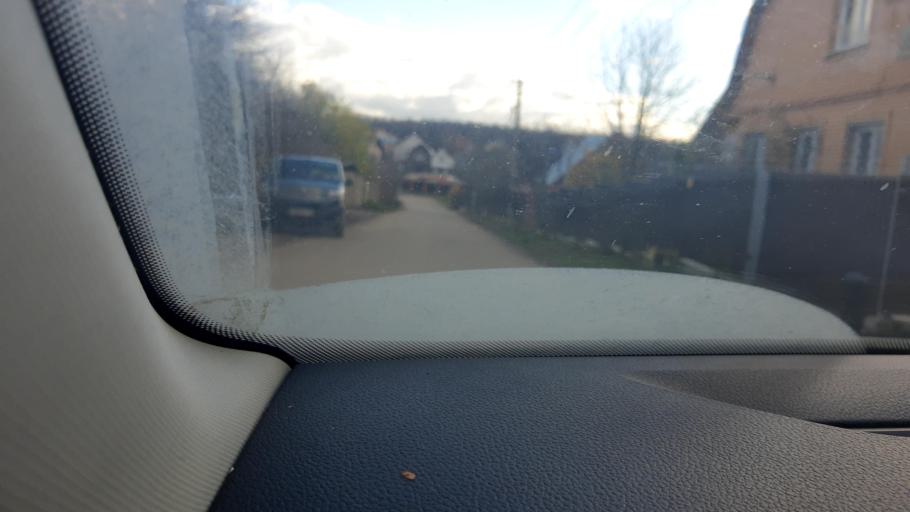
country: RU
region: Moscow
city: Annino
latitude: 55.5579
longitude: 37.6188
